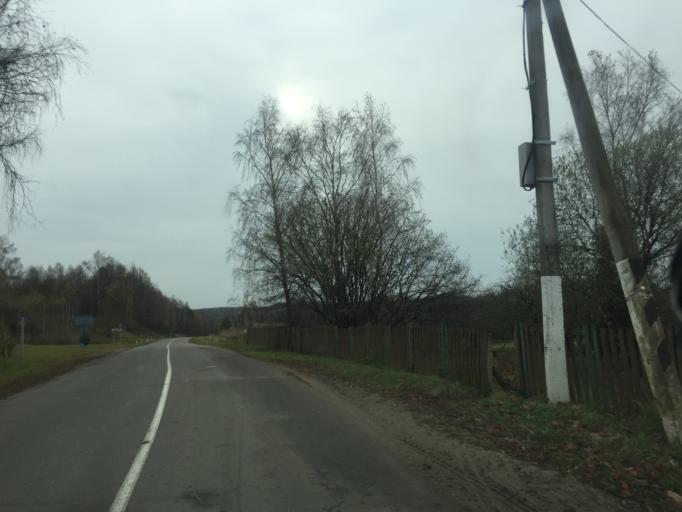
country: BY
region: Mogilev
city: Chavusy
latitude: 53.9579
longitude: 31.0363
